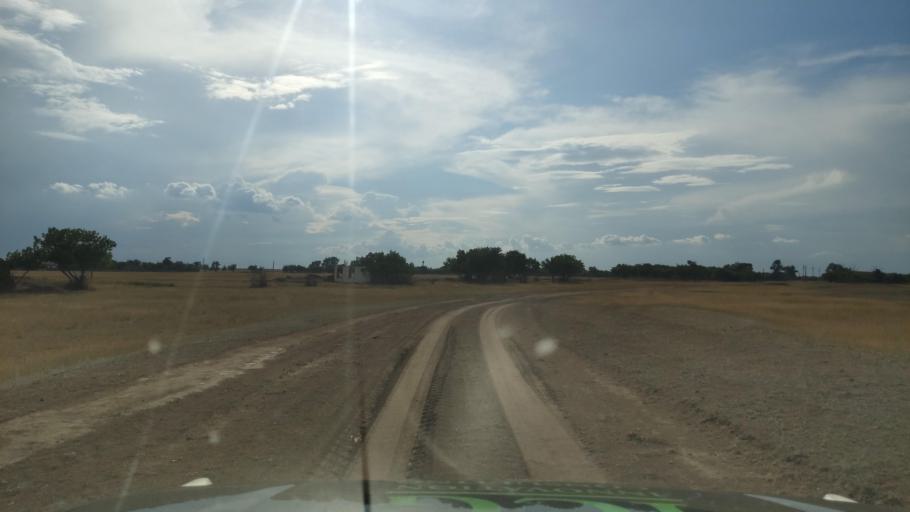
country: KZ
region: Pavlodar
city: Pavlodar
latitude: 52.5155
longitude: 77.4533
